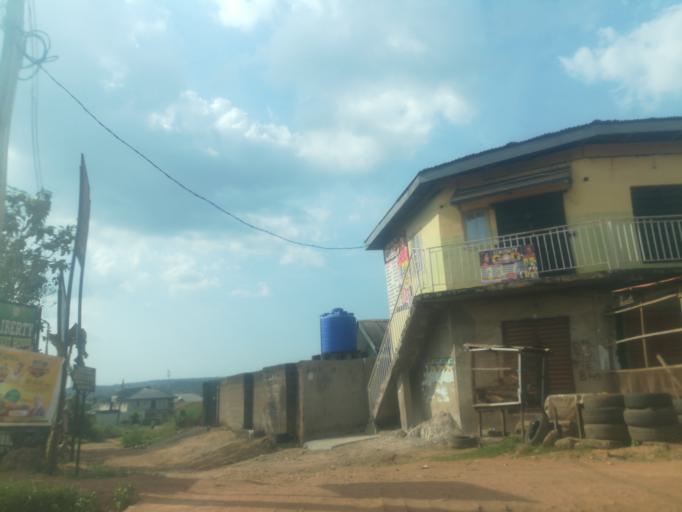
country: NG
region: Ogun
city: Abeokuta
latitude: 7.1158
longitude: 3.3159
